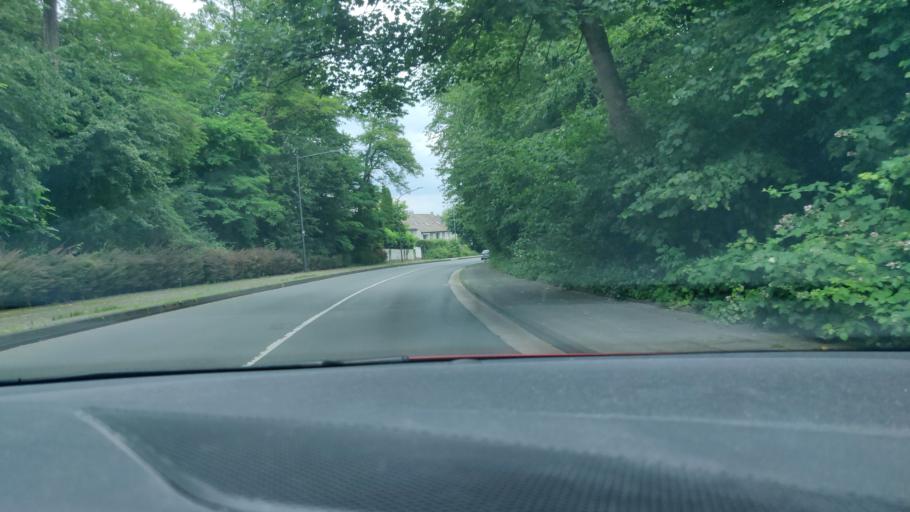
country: DE
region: North Rhine-Westphalia
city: Haan
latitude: 51.2225
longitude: 7.0598
